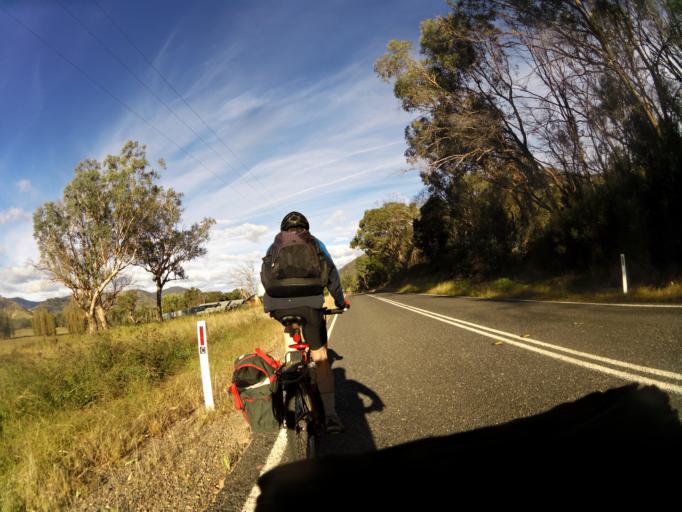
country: AU
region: New South Wales
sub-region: Greater Hume Shire
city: Holbrook
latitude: -35.9863
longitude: 147.8296
